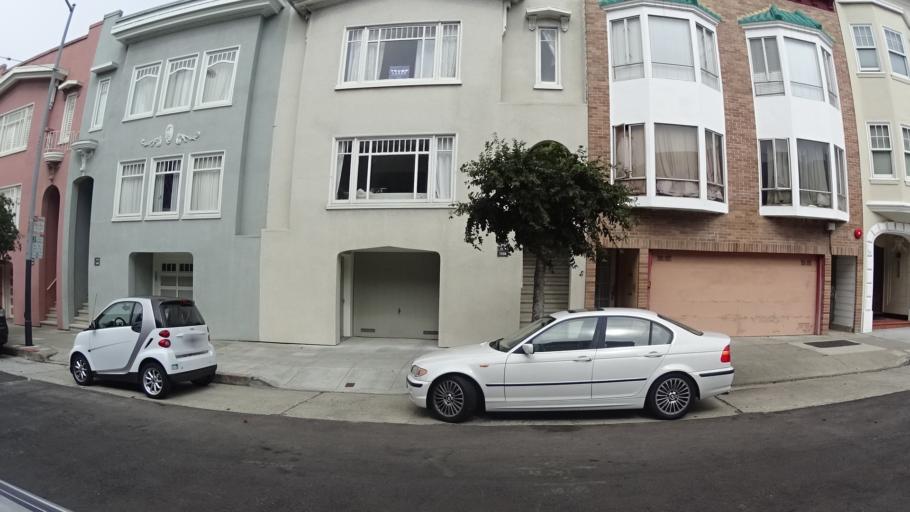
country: US
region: California
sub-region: San Francisco County
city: San Francisco
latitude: 37.8018
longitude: -122.4287
